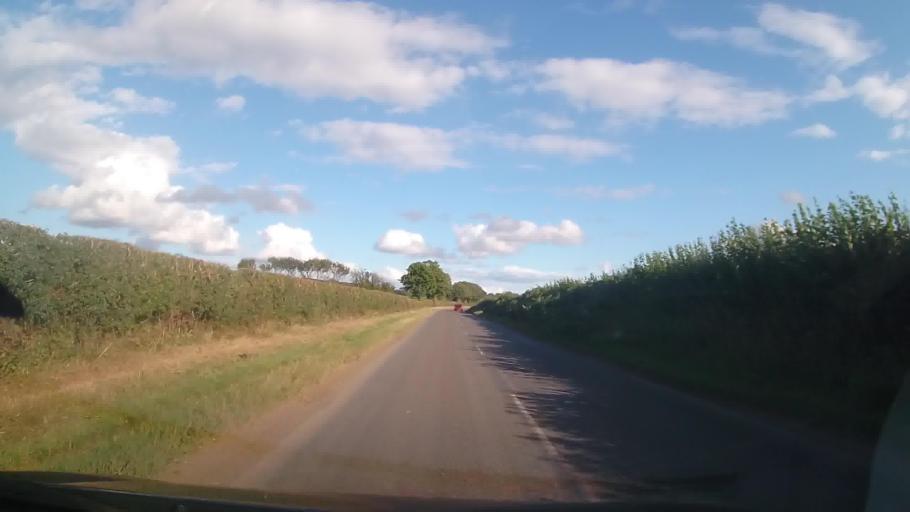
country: GB
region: England
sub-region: Shropshire
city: Great Hanwood
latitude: 52.6592
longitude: -2.8137
